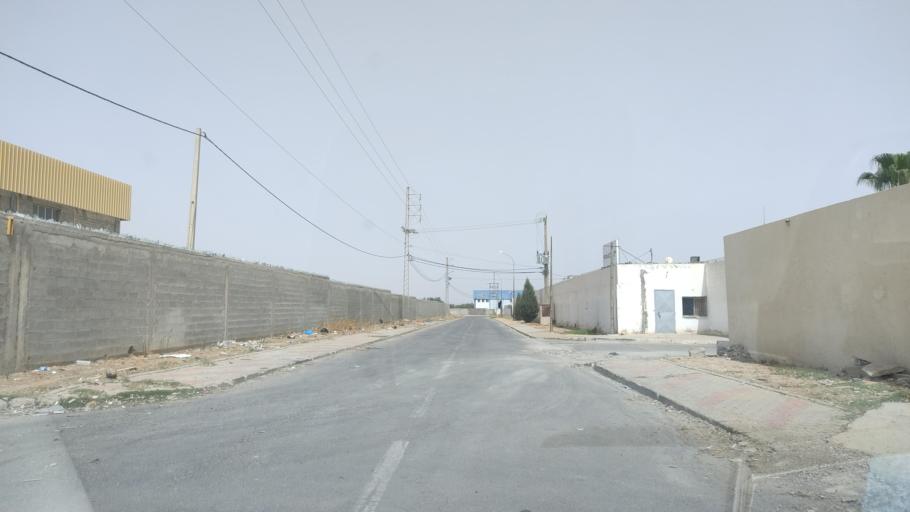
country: TN
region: Al Mahdiyah
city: El Jem
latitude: 35.1294
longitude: 10.7367
